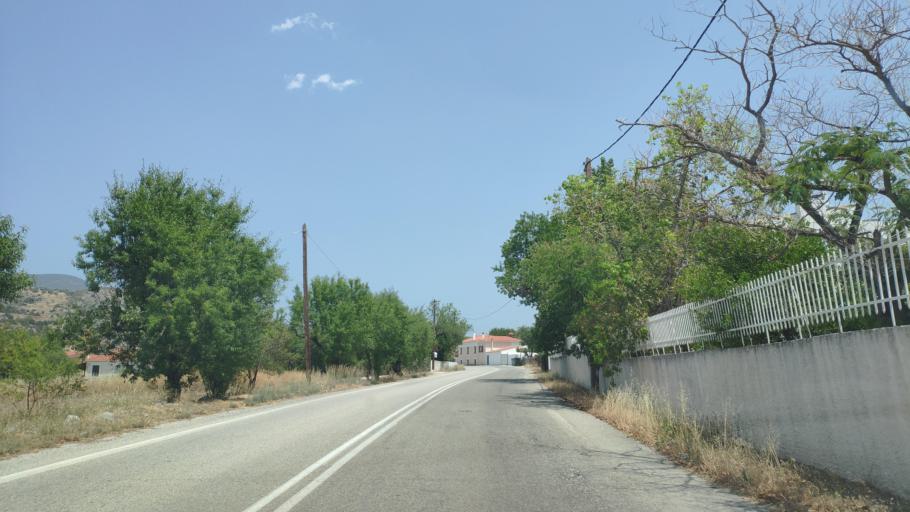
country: GR
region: Peloponnese
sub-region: Nomos Argolidos
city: Didyma
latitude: 37.4314
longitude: 23.1780
